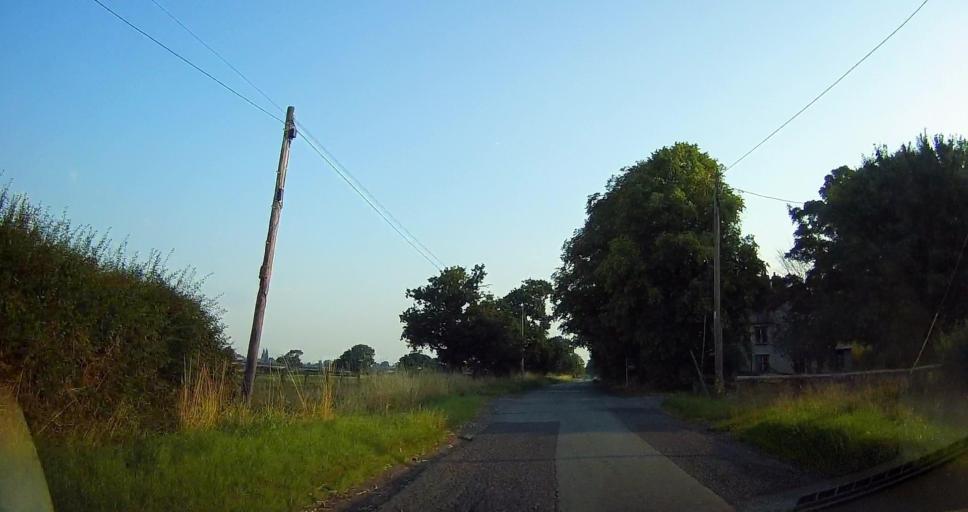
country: GB
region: England
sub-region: Cheshire East
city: Nantwich
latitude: 53.0229
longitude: -2.5211
